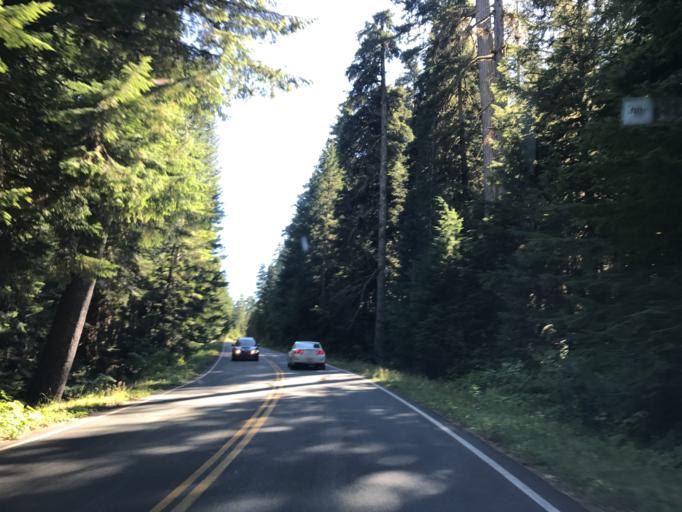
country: US
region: Washington
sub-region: Pierce County
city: Buckley
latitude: 46.7490
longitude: -121.5705
